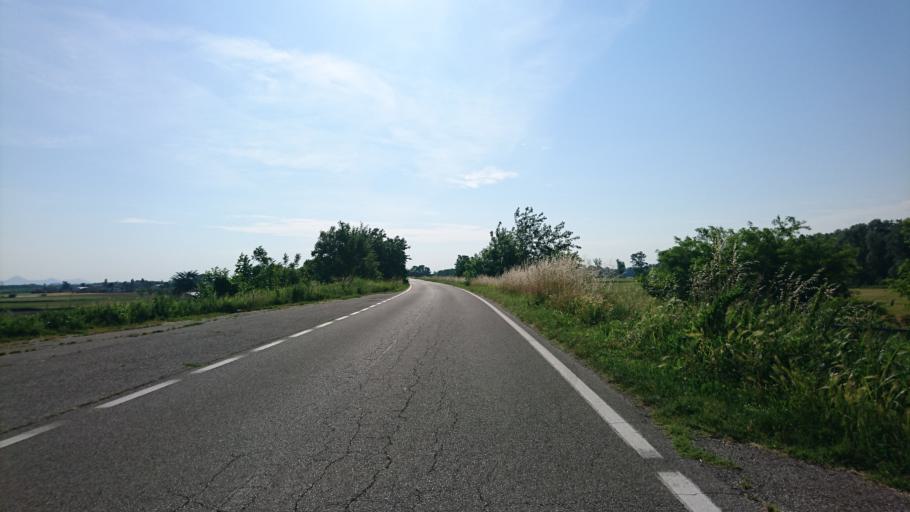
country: IT
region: Veneto
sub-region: Provincia di Verona
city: Villa Bartolomea
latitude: 45.1662
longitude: 11.3565
